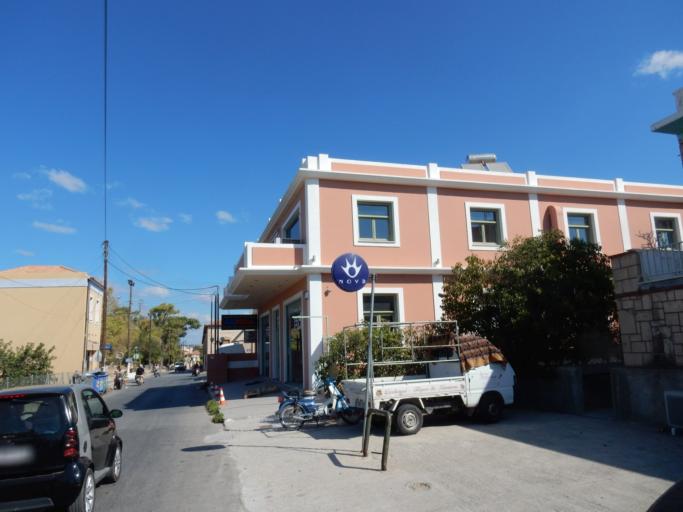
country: GR
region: Attica
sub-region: Nomos Piraios
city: Aegina
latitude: 37.7419
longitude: 23.4341
